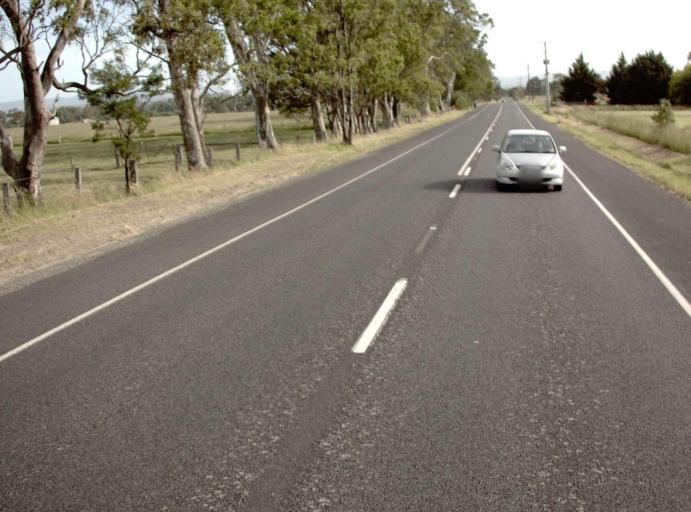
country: AU
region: Victoria
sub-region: Latrobe
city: Traralgon
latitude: -38.1430
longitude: 146.5561
